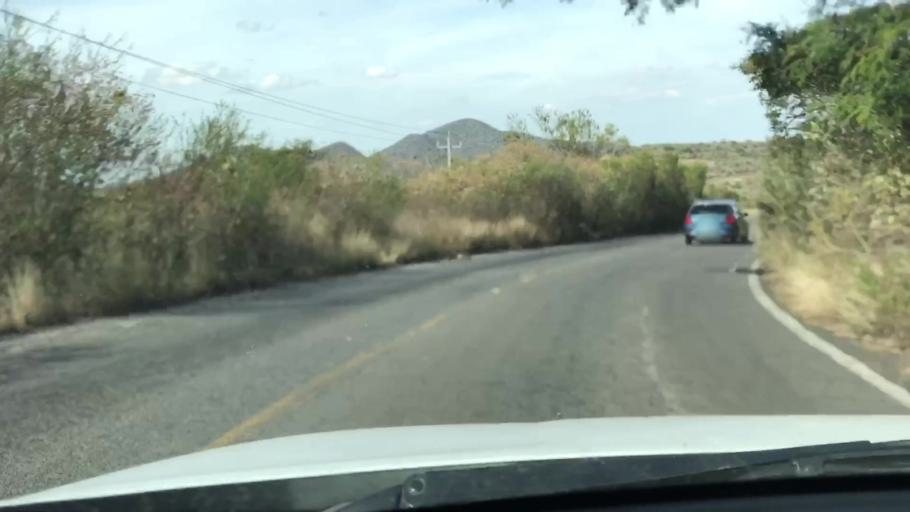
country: MX
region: Jalisco
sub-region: Zacoalco de Torres
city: Barranca de Otates (Barranca de Otatan)
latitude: 20.2334
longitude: -103.6854
